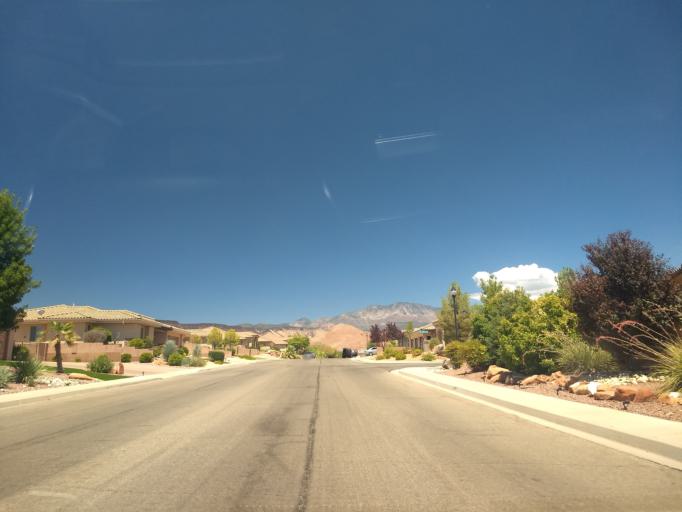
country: US
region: Utah
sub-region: Washington County
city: Washington
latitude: 37.1506
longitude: -113.5215
